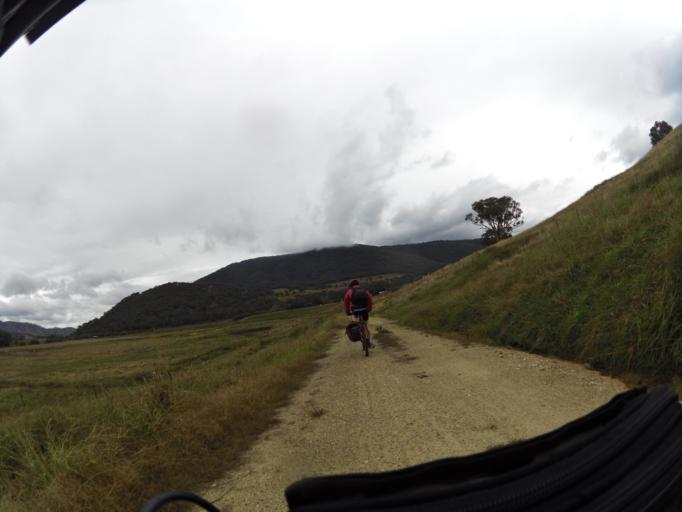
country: AU
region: New South Wales
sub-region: Albury Municipality
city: East Albury
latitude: -36.1825
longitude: 147.3491
